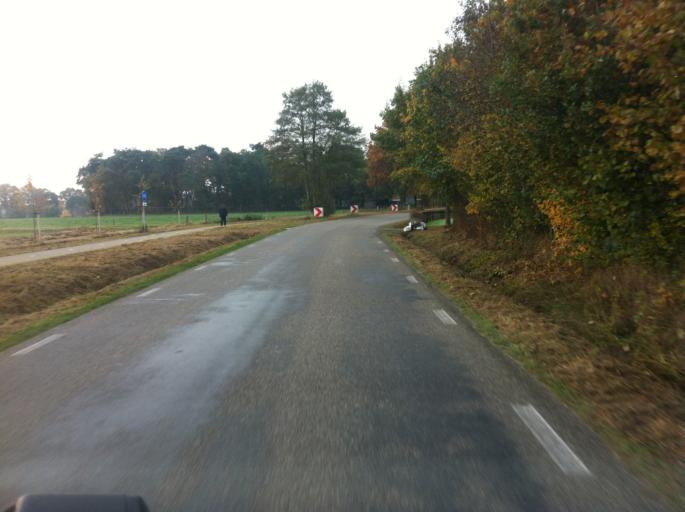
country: NL
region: Overijssel
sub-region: Gemeente Enschede
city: Enschede
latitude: 52.1681
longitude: 6.8792
